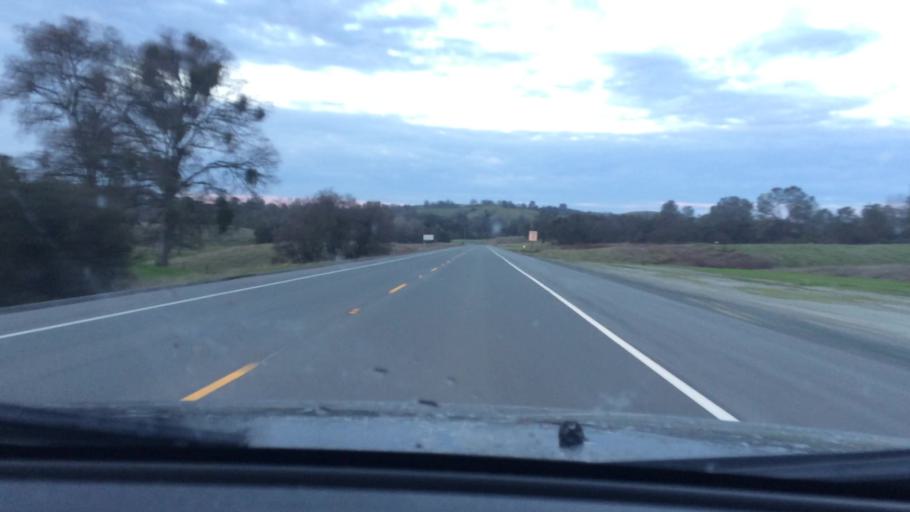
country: US
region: California
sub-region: Amador County
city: Ione
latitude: 38.3944
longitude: -120.9010
